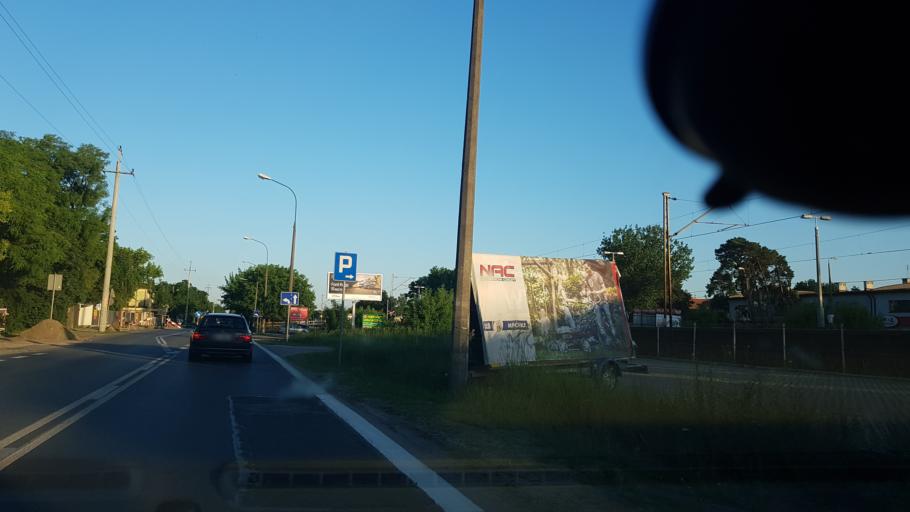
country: PL
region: Masovian Voivodeship
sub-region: Warszawa
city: Wawer
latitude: 52.1731
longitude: 21.2003
